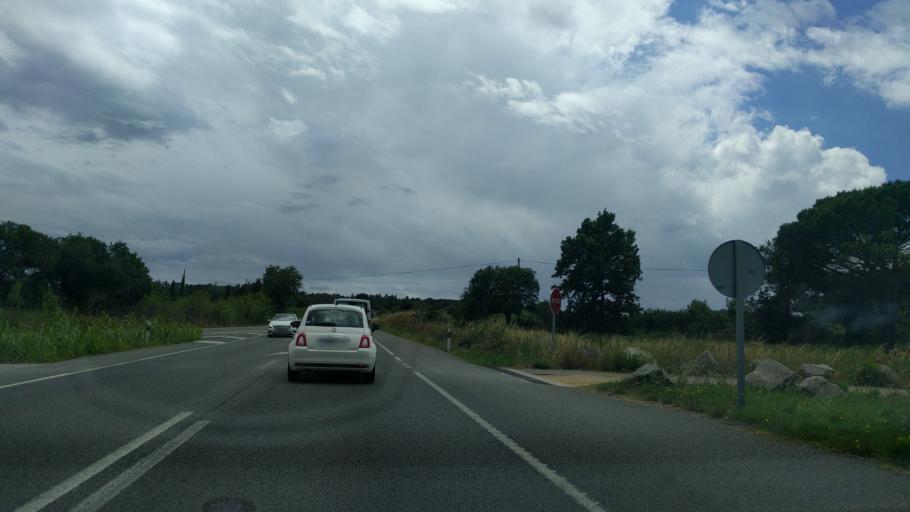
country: ES
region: Catalonia
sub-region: Provincia de Girona
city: Macanet de la Selva
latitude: 41.7556
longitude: 2.7563
